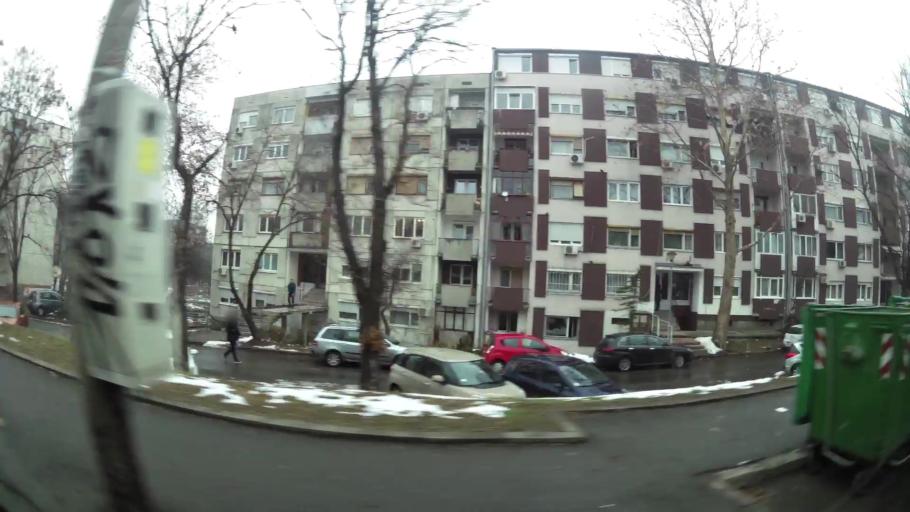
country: RS
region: Central Serbia
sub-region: Belgrade
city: Vozdovac
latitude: 44.7767
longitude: 20.4810
